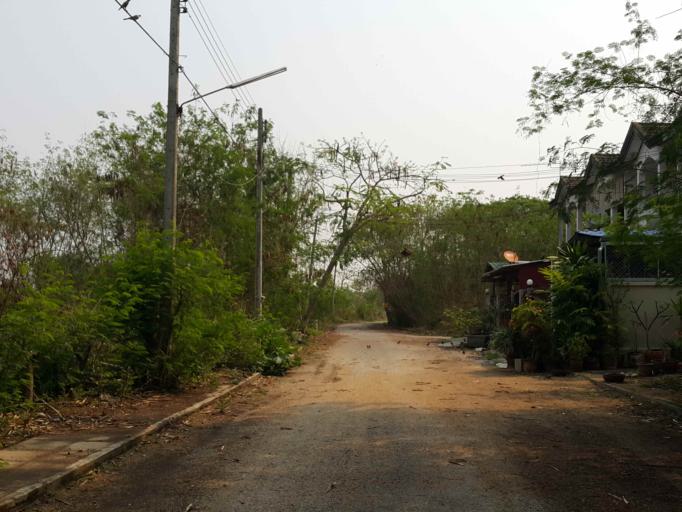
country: TH
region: Chiang Mai
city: Saraphi
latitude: 18.7617
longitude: 99.0609
